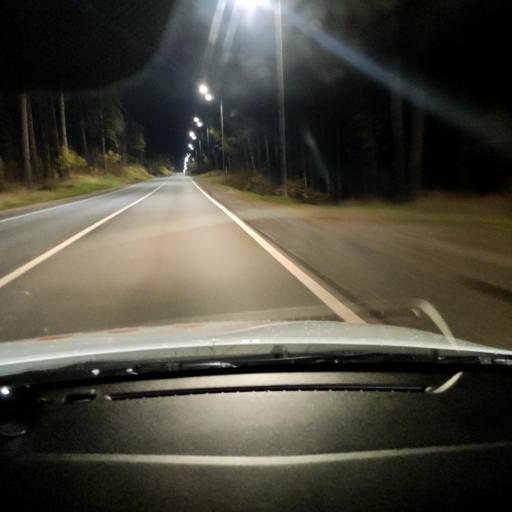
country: RU
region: Tatarstan
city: Verkhniy Uslon
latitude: 55.6375
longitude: 49.0505
